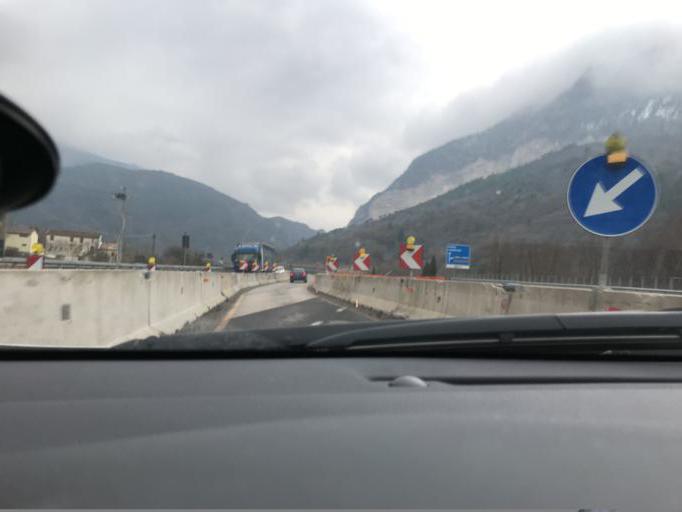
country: IT
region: The Marches
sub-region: Provincia di Ancona
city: Serra San Quirico
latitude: 43.4393
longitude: 13.0240
